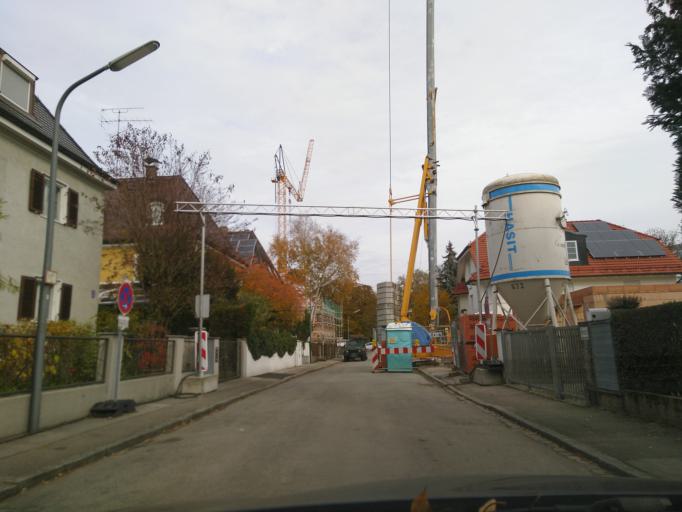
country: DE
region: Bavaria
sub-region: Upper Bavaria
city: Munich
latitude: 48.1095
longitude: 11.6012
